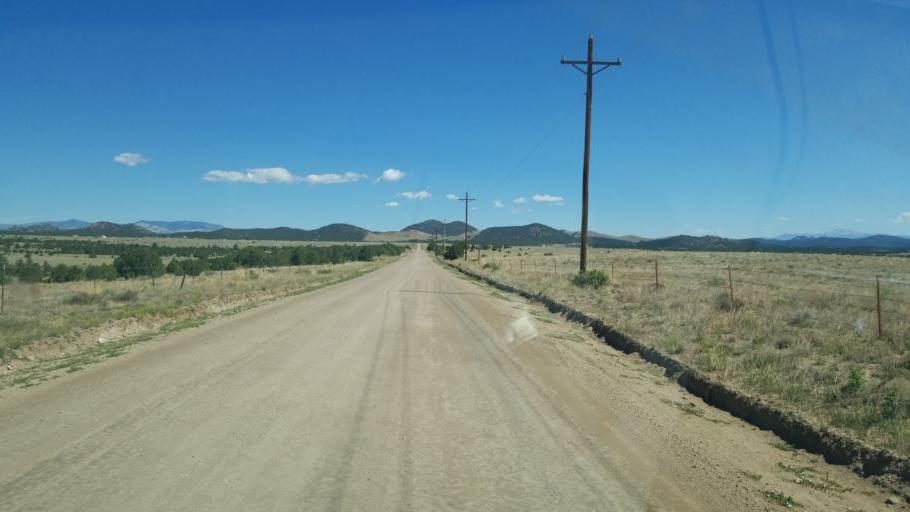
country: US
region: Colorado
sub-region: Custer County
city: Westcliffe
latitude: 38.2636
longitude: -105.5011
